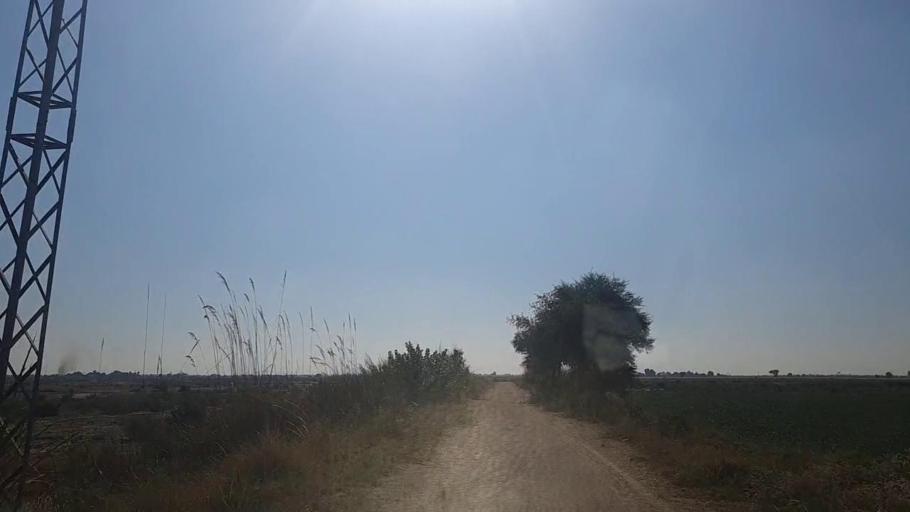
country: PK
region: Sindh
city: Sinjhoro
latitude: 26.1556
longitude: 68.8601
